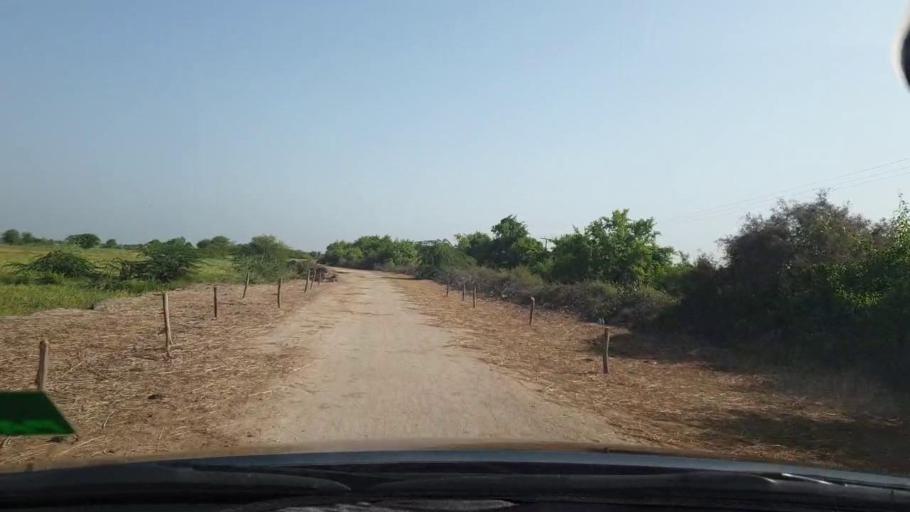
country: PK
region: Sindh
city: Tando Bago
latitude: 24.7218
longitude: 68.9961
